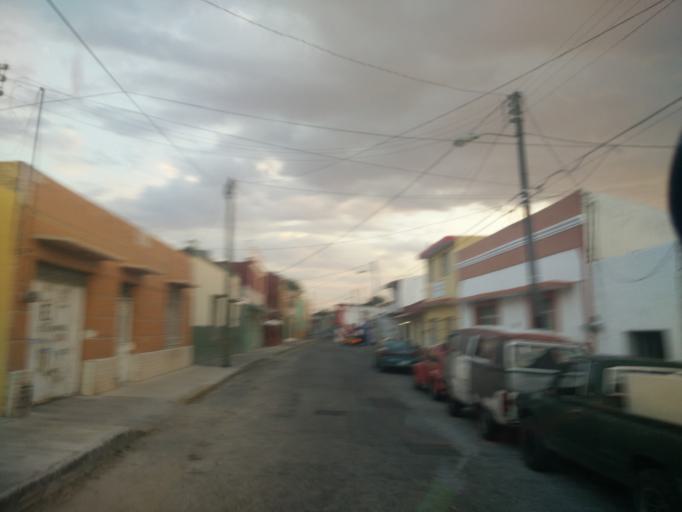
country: MX
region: Yucatan
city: Merida
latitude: 20.9630
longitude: -89.6098
